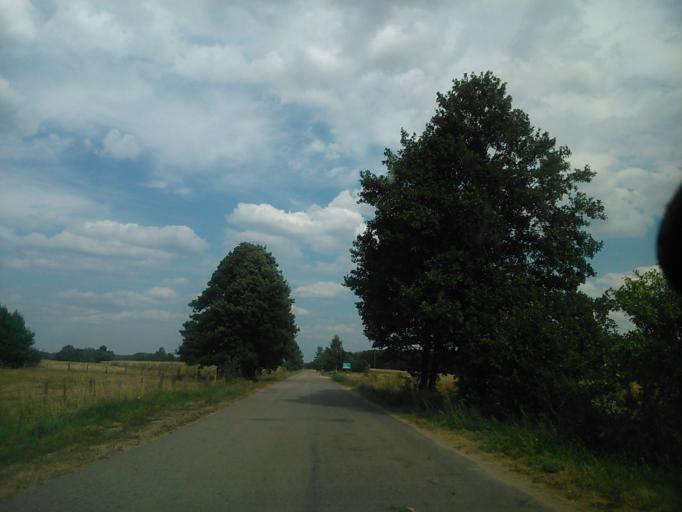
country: PL
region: Masovian Voivodeship
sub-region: Powiat ostrolecki
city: Czarnia
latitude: 53.3828
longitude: 21.2009
